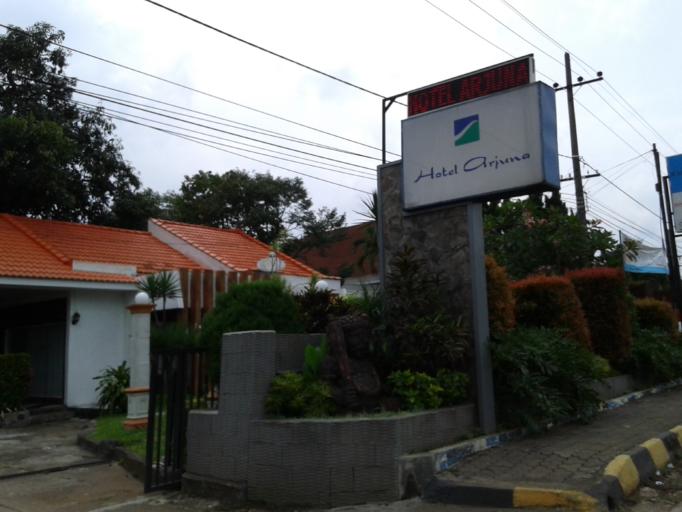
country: ID
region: East Java
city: Lawang
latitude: -7.8408
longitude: 112.6976
